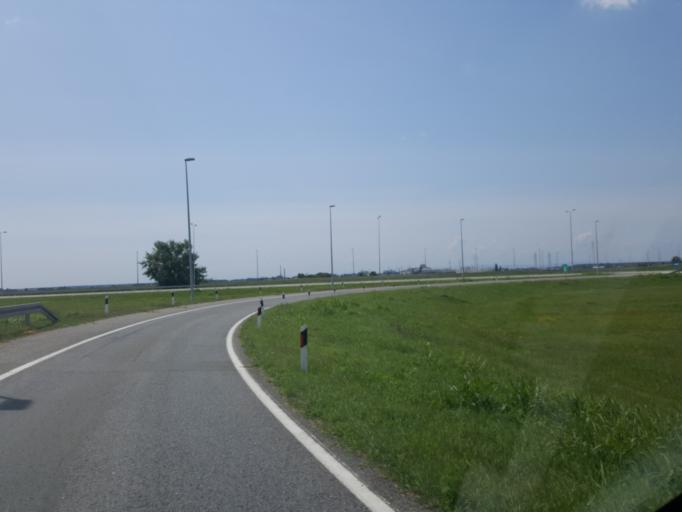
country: RS
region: Autonomna Pokrajina Vojvodina
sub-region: Sremski Okrug
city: Sremska Mitrovica
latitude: 45.0002
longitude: 19.6531
